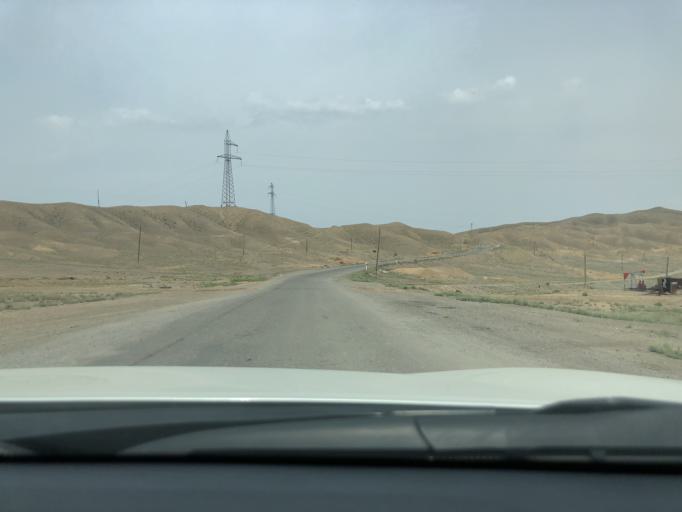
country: TJ
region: Viloyati Sughd
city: Kim
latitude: 40.2150
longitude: 70.4759
